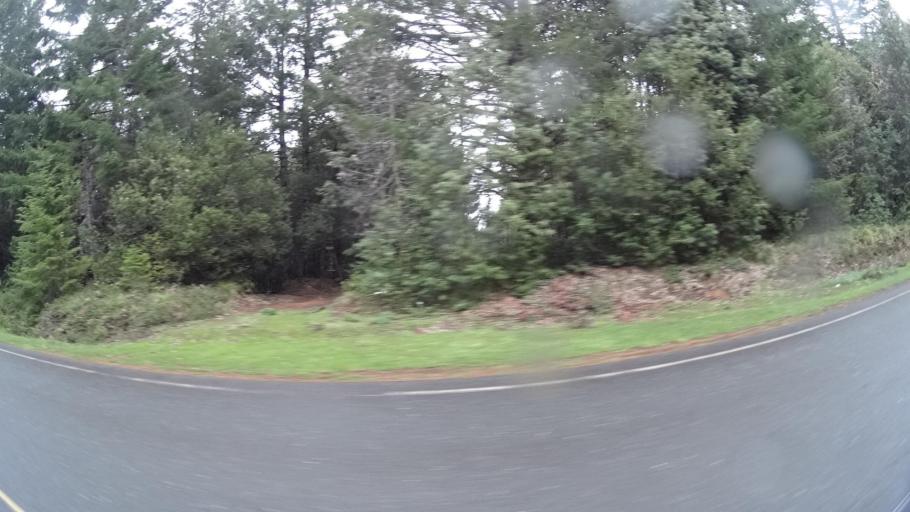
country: US
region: California
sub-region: Humboldt County
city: Willow Creek
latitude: 41.1855
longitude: -123.8149
